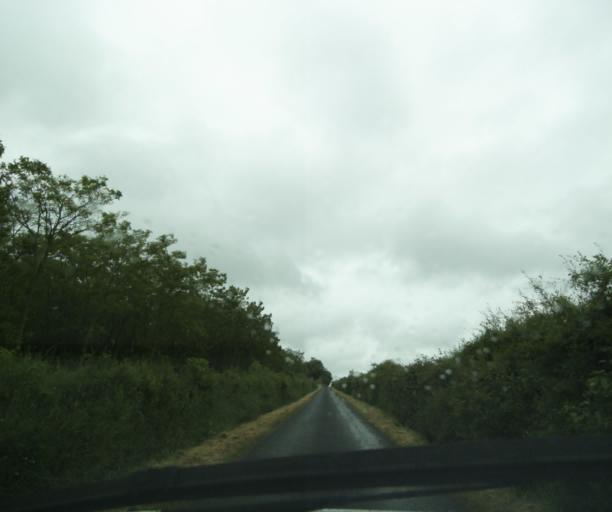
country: FR
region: Bourgogne
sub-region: Departement de Saone-et-Loire
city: Saint-Vallier
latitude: 46.4927
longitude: 4.4725
